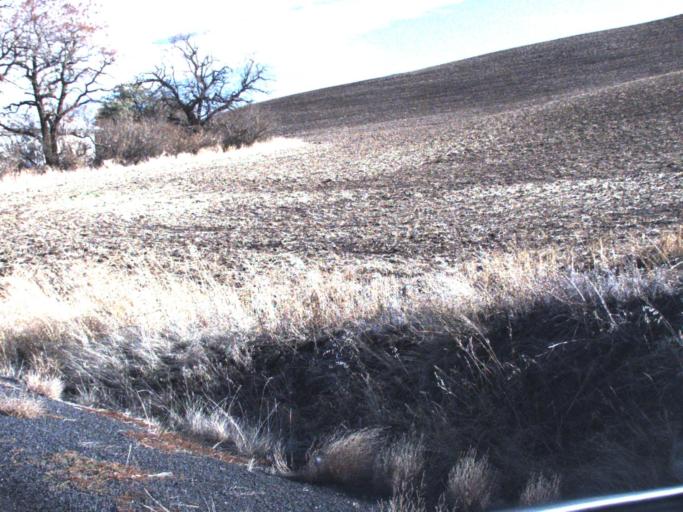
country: US
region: Washington
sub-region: Whitman County
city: Colfax
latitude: 46.9034
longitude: -117.2961
